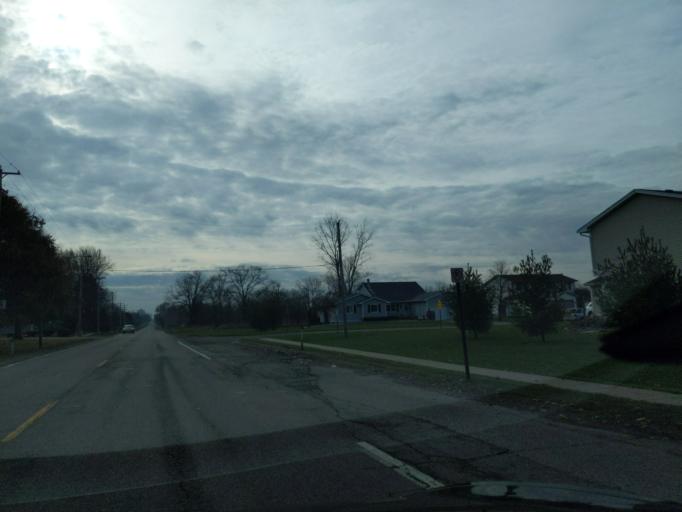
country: US
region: Michigan
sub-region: Ingham County
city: Holt
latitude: 42.6289
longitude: -84.5233
